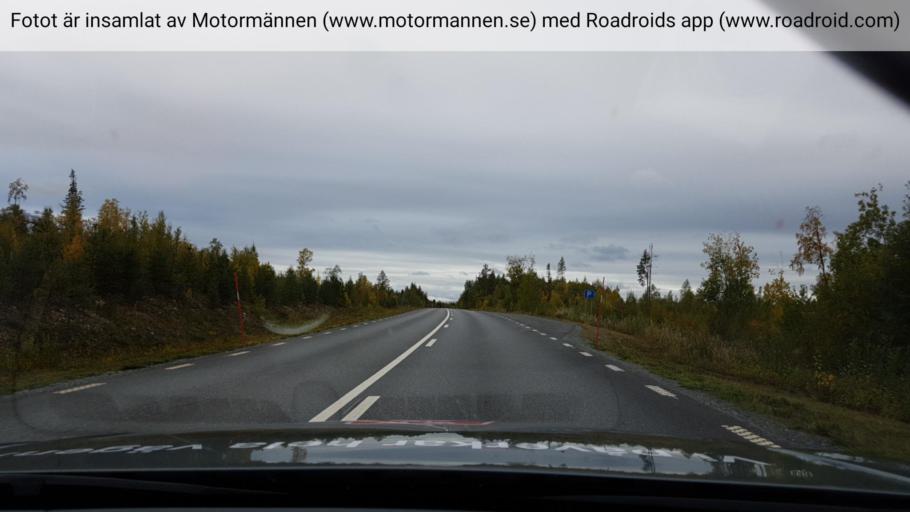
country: SE
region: Vaesterbotten
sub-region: Dorotea Kommun
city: Dorotea
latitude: 64.3192
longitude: 16.6120
